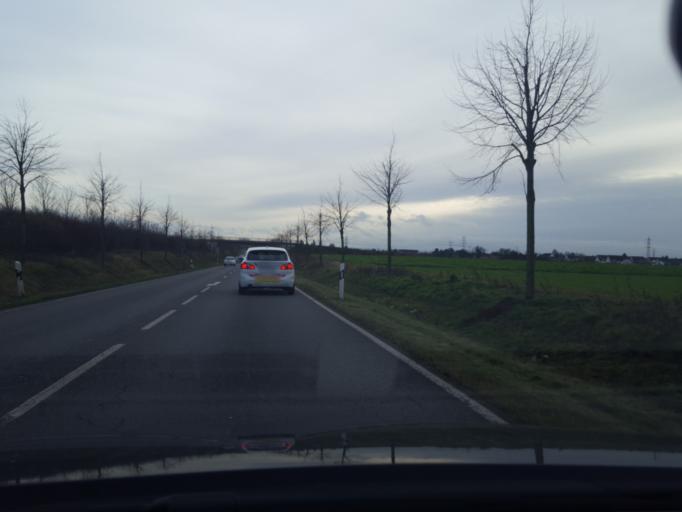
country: DE
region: North Rhine-Westphalia
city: Niederkassel
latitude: 50.8245
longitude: 7.0448
